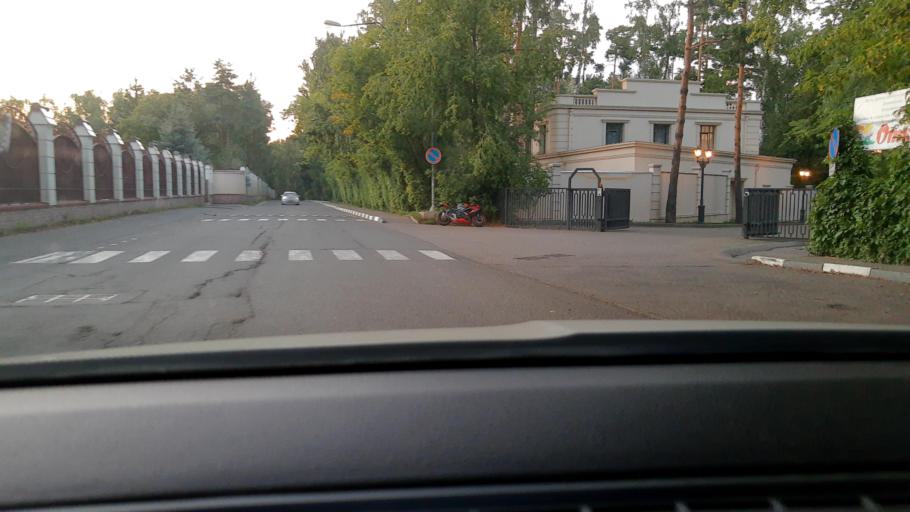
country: RU
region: Moskovskaya
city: Zarech'ye
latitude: 55.6838
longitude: 37.3845
